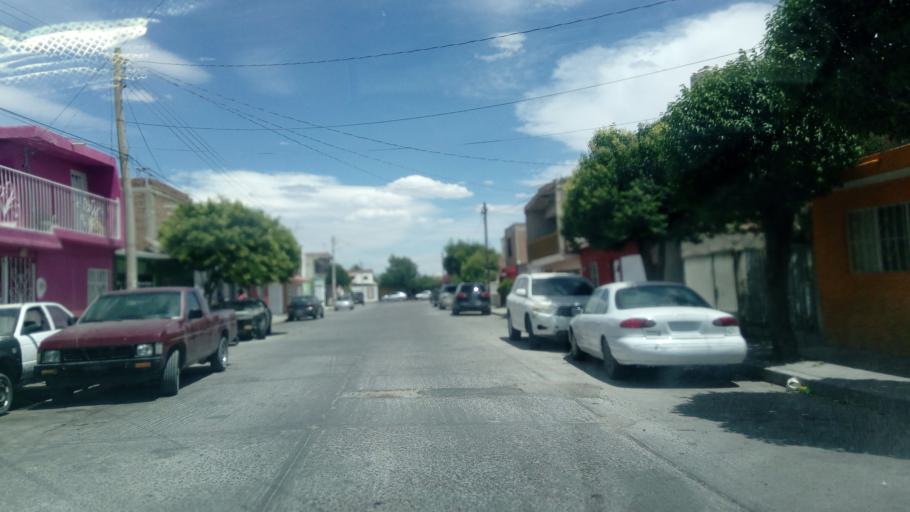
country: MX
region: Durango
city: Victoria de Durango
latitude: 24.0002
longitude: -104.6759
